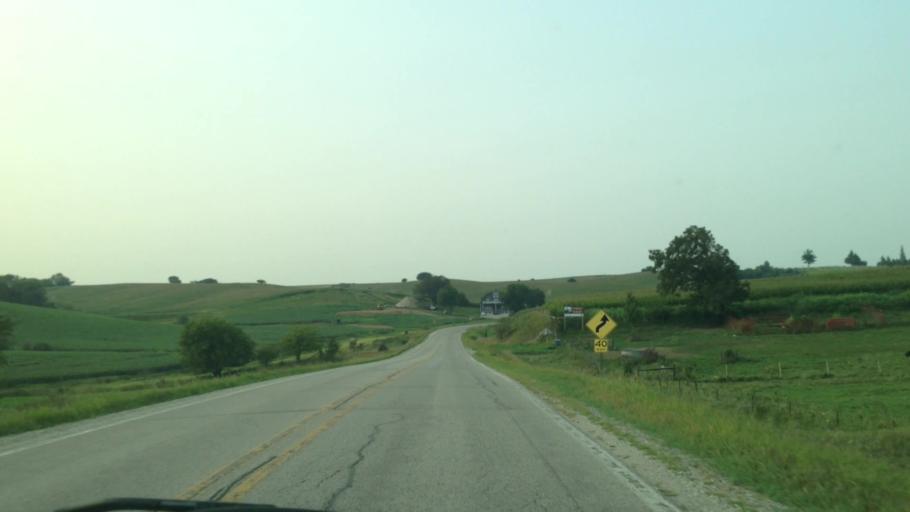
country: US
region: Iowa
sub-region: Iowa County
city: Marengo
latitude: 41.8797
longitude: -92.0890
